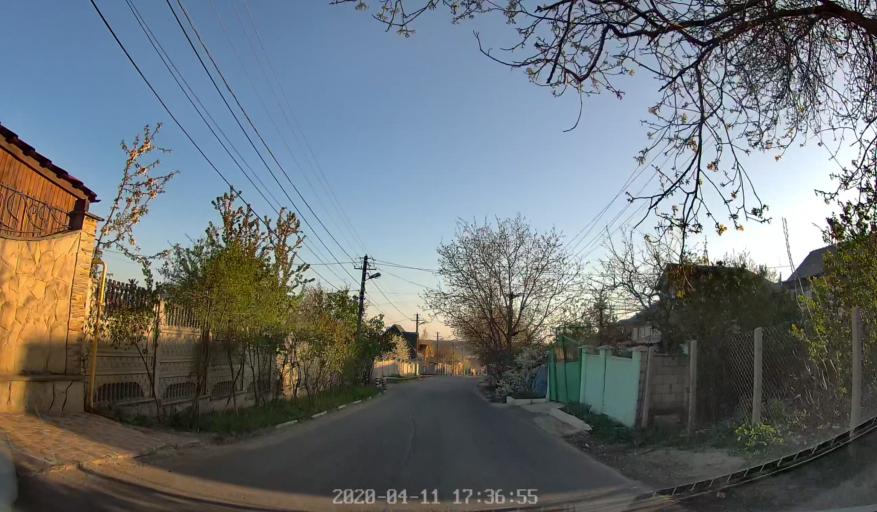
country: MD
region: Laloveni
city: Ialoveni
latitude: 46.9815
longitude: 28.8027
